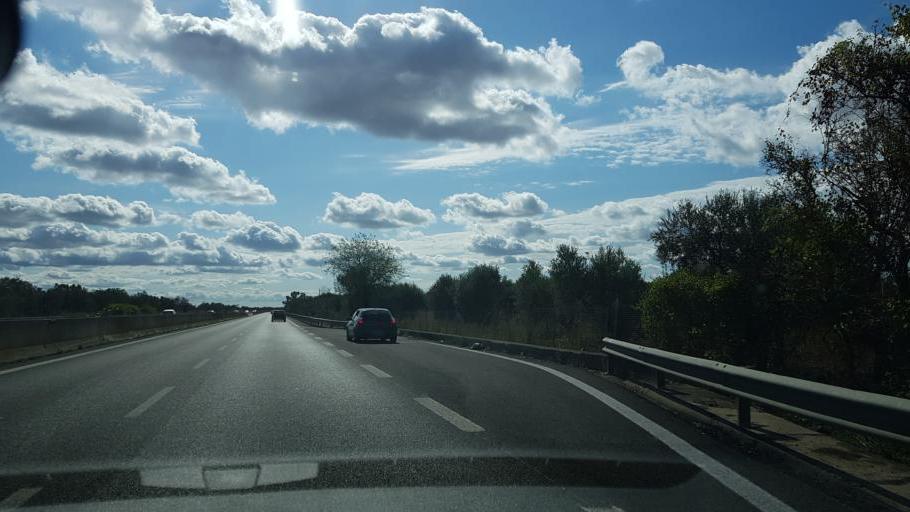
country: IT
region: Apulia
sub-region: Provincia di Lecce
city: Trepuzzi
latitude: 40.4145
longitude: 18.1016
